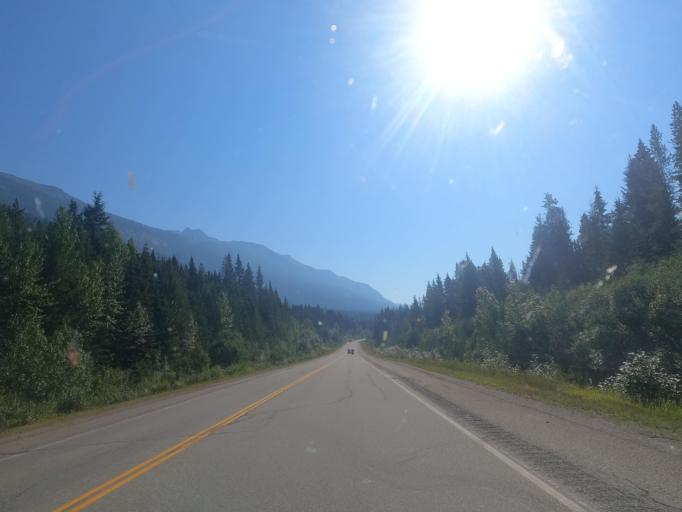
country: CA
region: Alberta
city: Grande Cache
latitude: 53.0024
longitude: -119.0414
